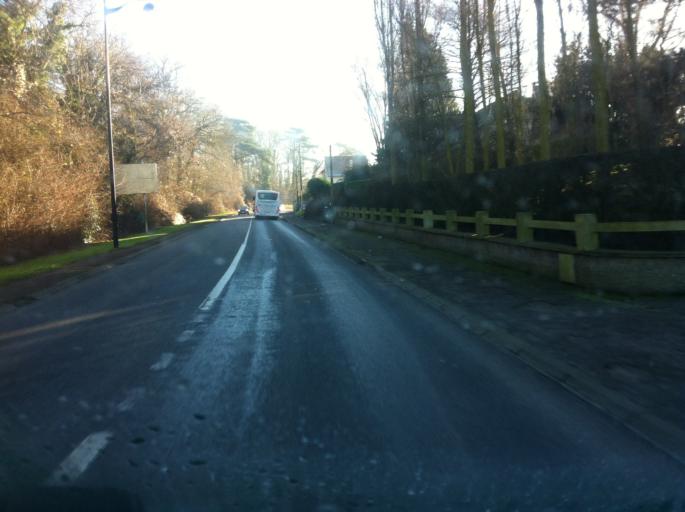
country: FR
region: Picardie
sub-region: Departement de la Somme
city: Mers-les-Bains
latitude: 50.0526
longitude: 1.3999
